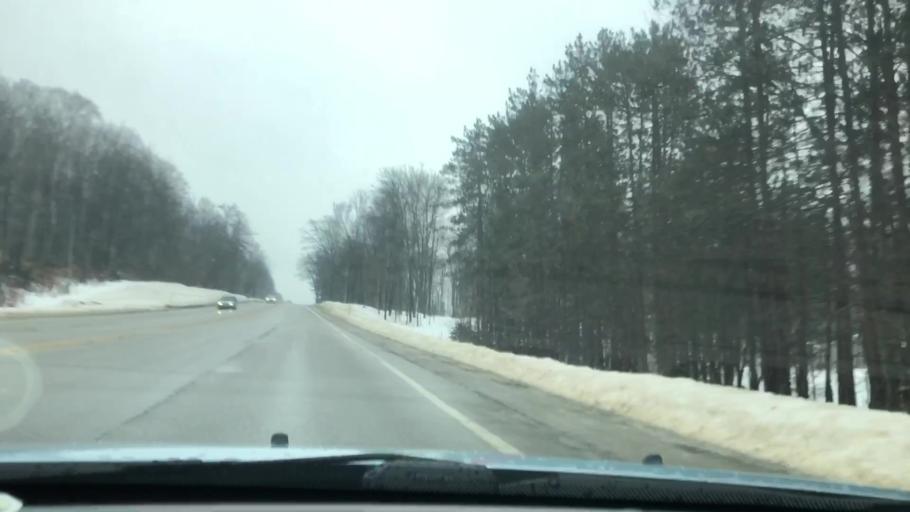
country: US
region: Michigan
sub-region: Otsego County
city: Gaylord
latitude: 45.0390
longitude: -84.7759
